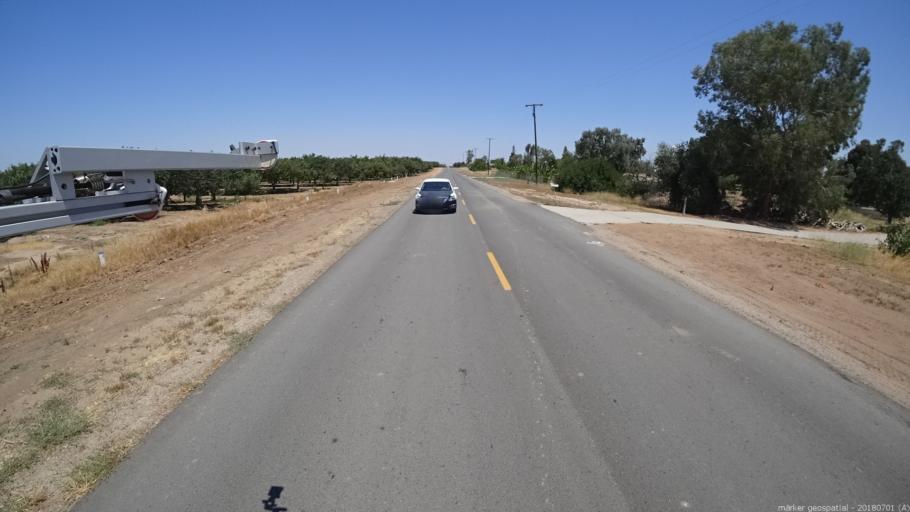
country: US
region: California
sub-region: Madera County
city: Madera Acres
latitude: 37.0478
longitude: -120.0019
